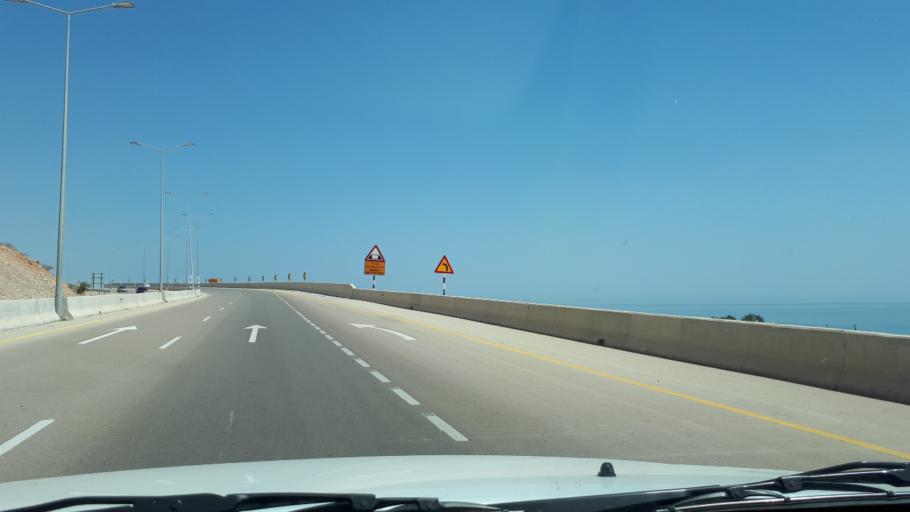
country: OM
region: Ash Sharqiyah
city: Sur
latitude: 22.8189
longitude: 59.2620
